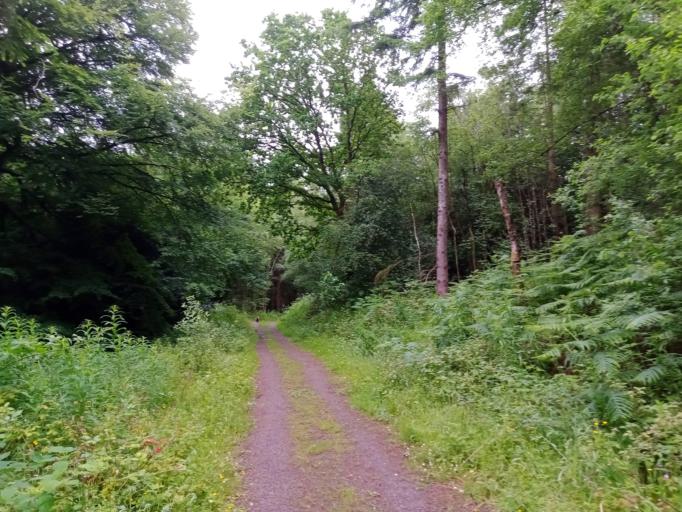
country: IE
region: Leinster
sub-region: Kilkenny
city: Piltown
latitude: 52.4485
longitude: -7.2736
